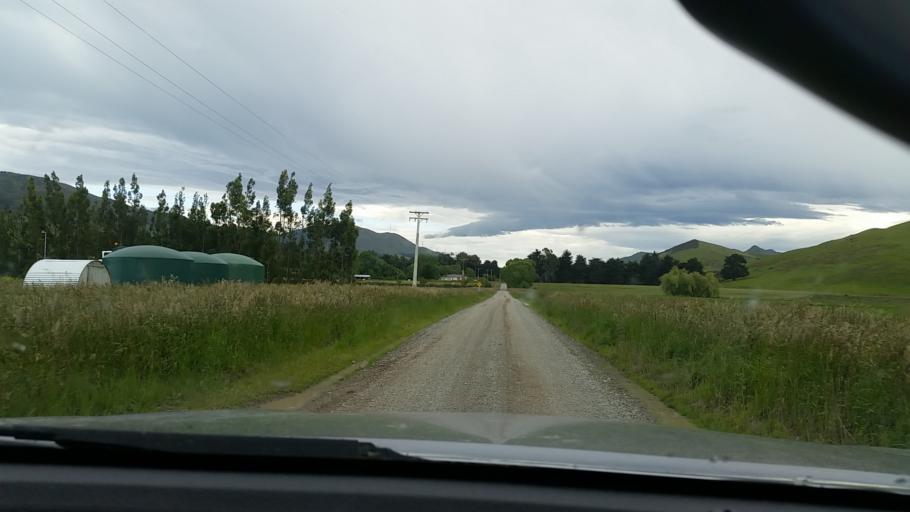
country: NZ
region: Southland
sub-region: Southland District
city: Winton
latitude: -45.7976
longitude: 168.3774
